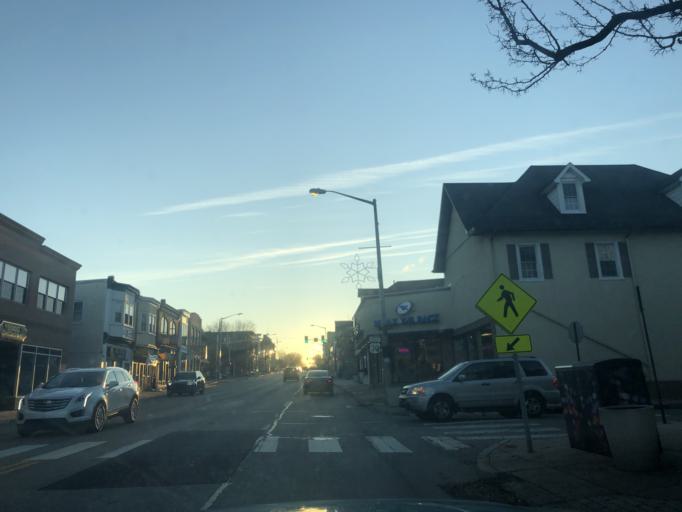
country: US
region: Pennsylvania
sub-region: Montgomery County
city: Bryn Mawr
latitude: 40.0240
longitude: -75.3236
